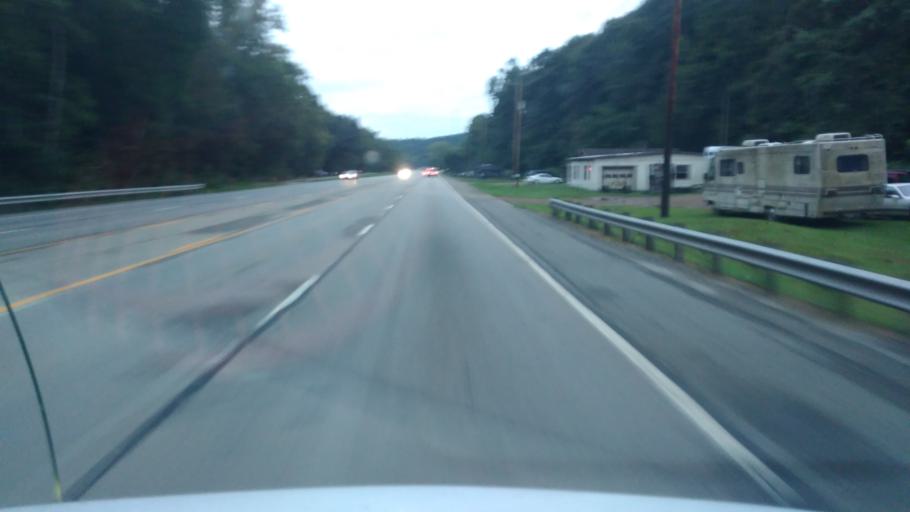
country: US
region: Ohio
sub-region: Pike County
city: Waverly
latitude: 39.1931
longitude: -82.9782
